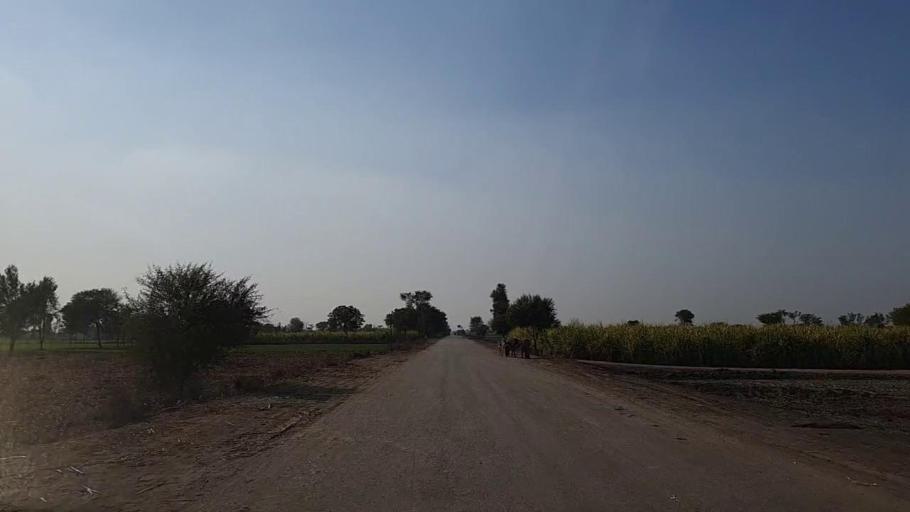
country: PK
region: Sindh
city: Daur
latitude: 26.4039
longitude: 68.2844
